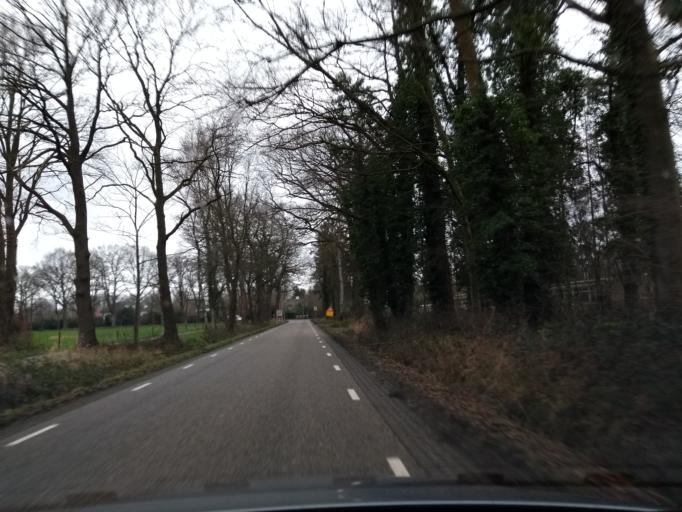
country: NL
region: Overijssel
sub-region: Gemeente Enschede
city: Enschede
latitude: 52.2126
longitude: 6.9298
